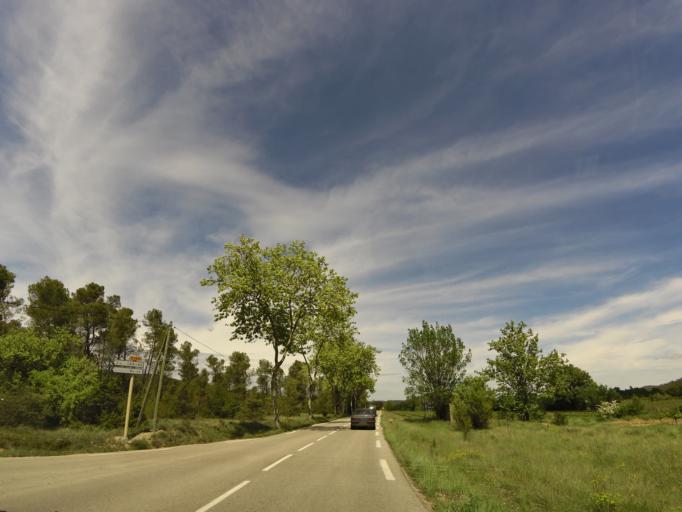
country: FR
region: Languedoc-Roussillon
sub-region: Departement du Gard
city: Quissac
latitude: 43.8570
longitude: 4.0169
